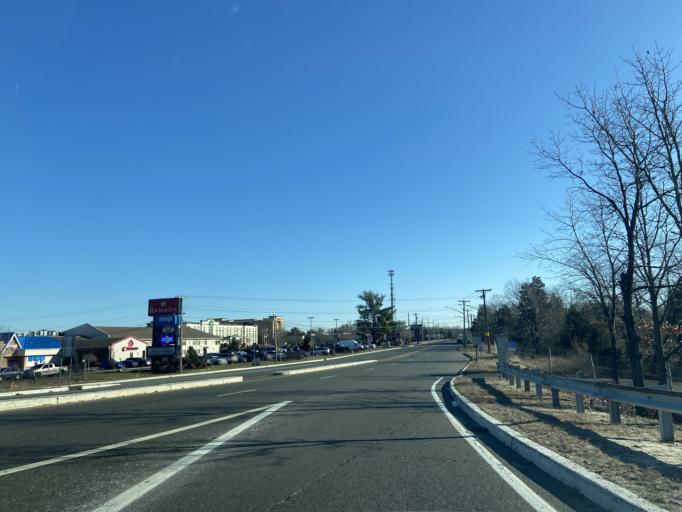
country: US
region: New Jersey
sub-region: Cumberland County
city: Vineland
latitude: 39.4881
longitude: -75.0695
